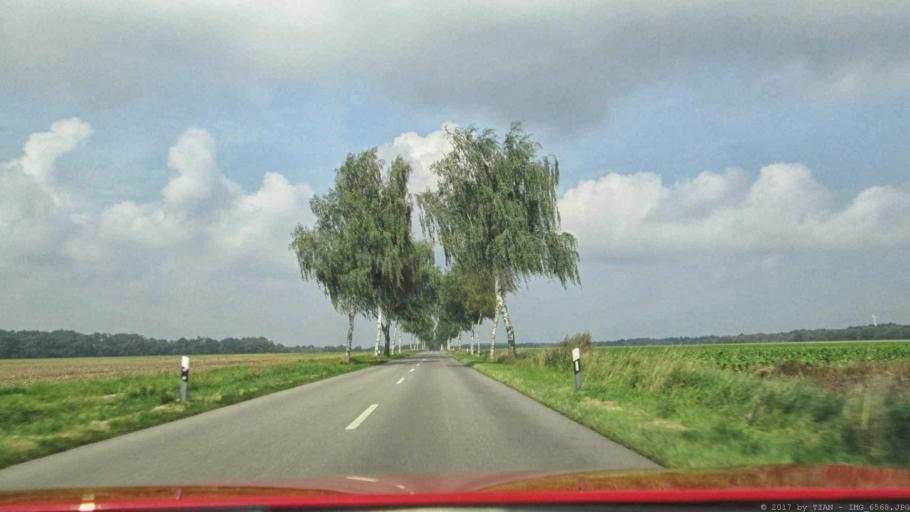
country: DE
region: Lower Saxony
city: Wrestedt
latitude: 52.9109
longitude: 10.5713
